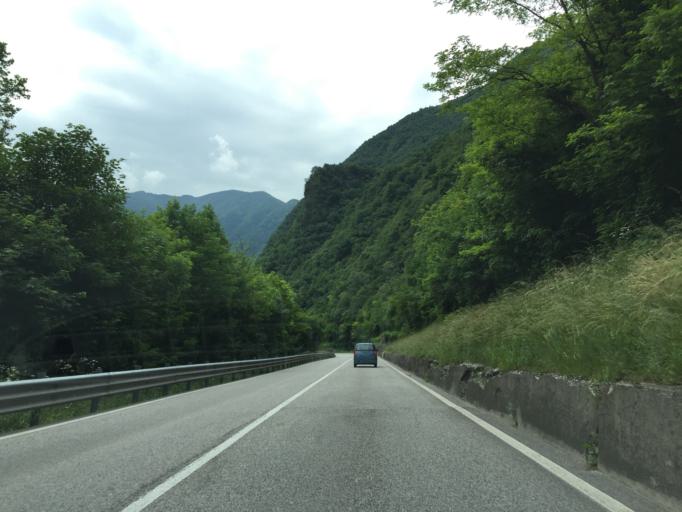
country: IT
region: Veneto
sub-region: Provincia di Belluno
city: Feltre
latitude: 45.9979
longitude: 11.9484
